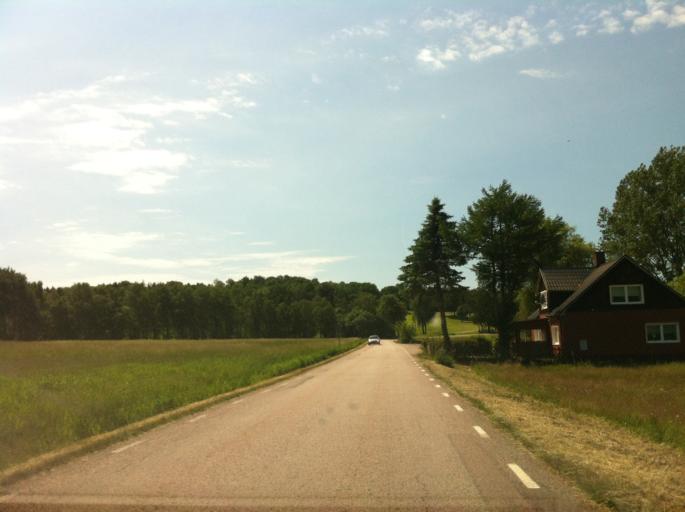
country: SE
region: Skane
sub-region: Bjuvs Kommun
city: Bjuv
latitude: 56.0620
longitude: 12.9508
